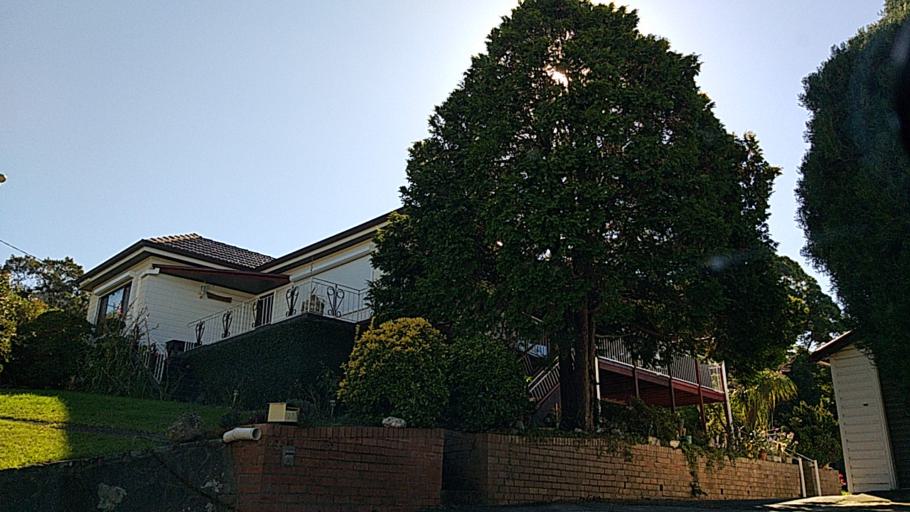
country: AU
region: New South Wales
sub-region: Wollongong
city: Bulli
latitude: -34.3112
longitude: 150.9249
